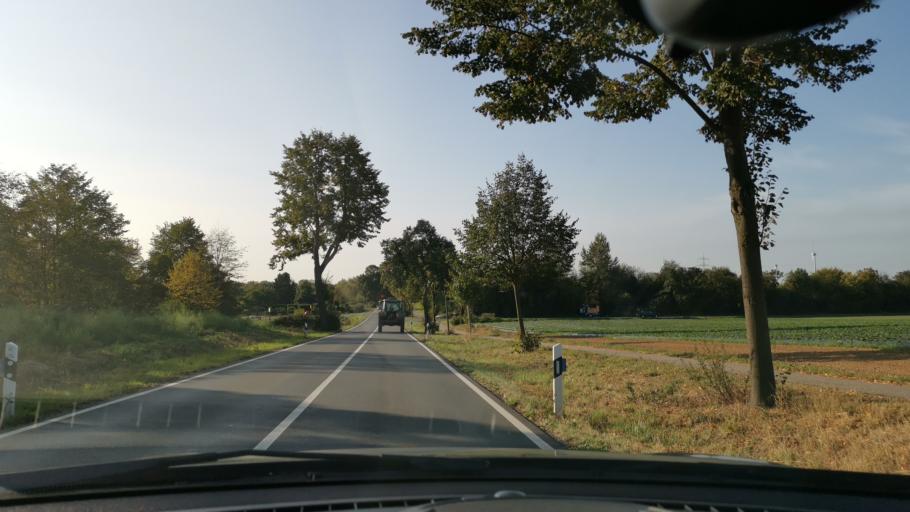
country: DE
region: North Rhine-Westphalia
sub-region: Regierungsbezirk Dusseldorf
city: Rommerskirchen
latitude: 51.0922
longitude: 6.7197
